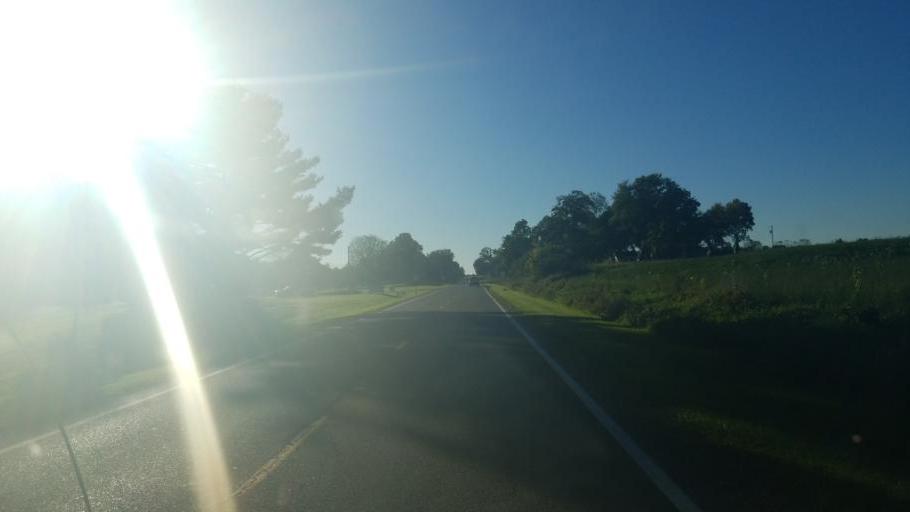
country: US
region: Ohio
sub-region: Columbiana County
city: Columbiana
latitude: 40.9003
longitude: -80.7105
